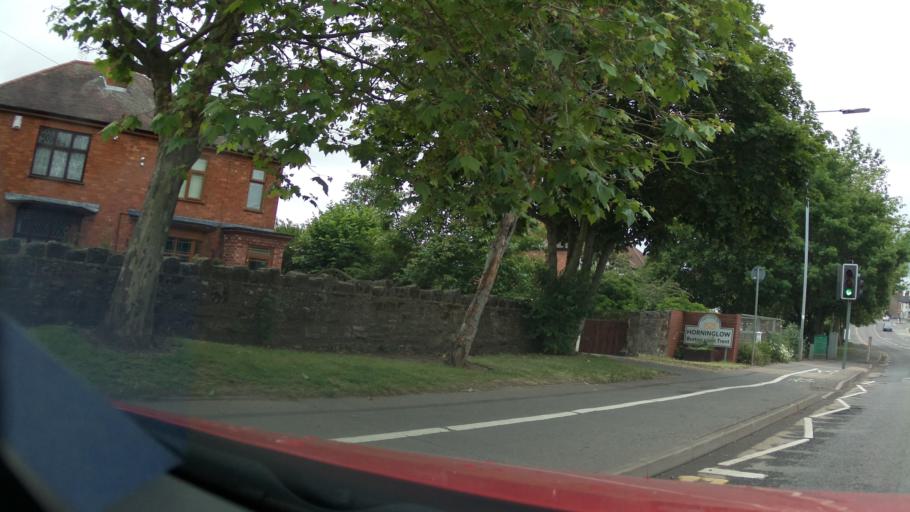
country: GB
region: England
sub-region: Staffordshire
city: Burton upon Trent
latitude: 52.8273
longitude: -1.6505
